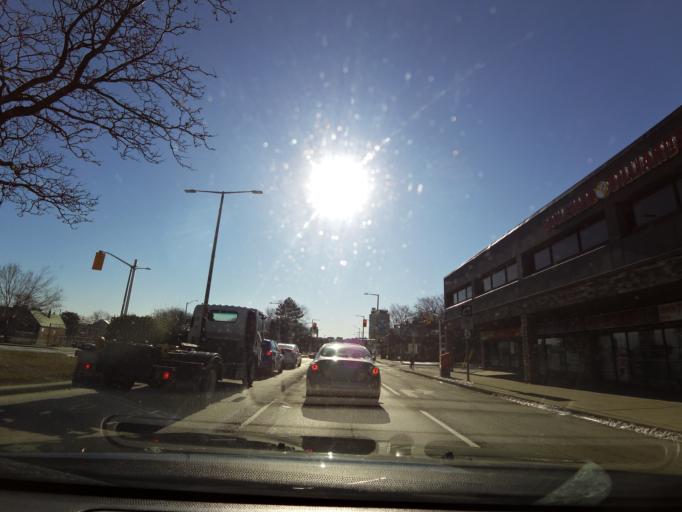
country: CA
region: Ontario
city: Hamilton
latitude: 43.2630
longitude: -79.8777
